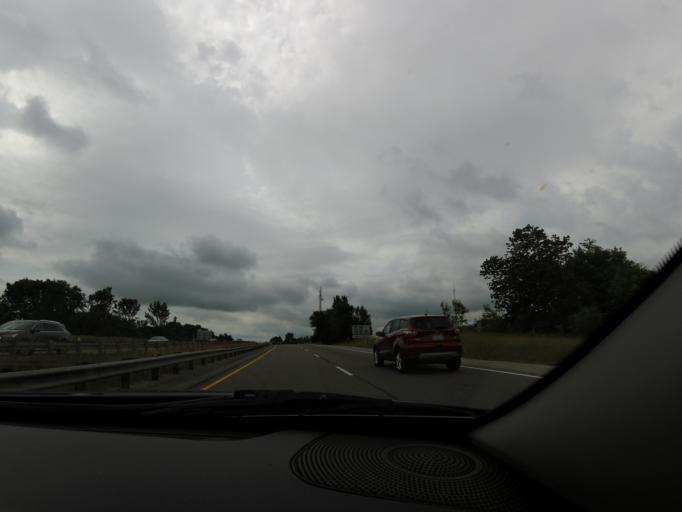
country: CA
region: Ontario
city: Orillia
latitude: 44.5995
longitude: -79.4476
